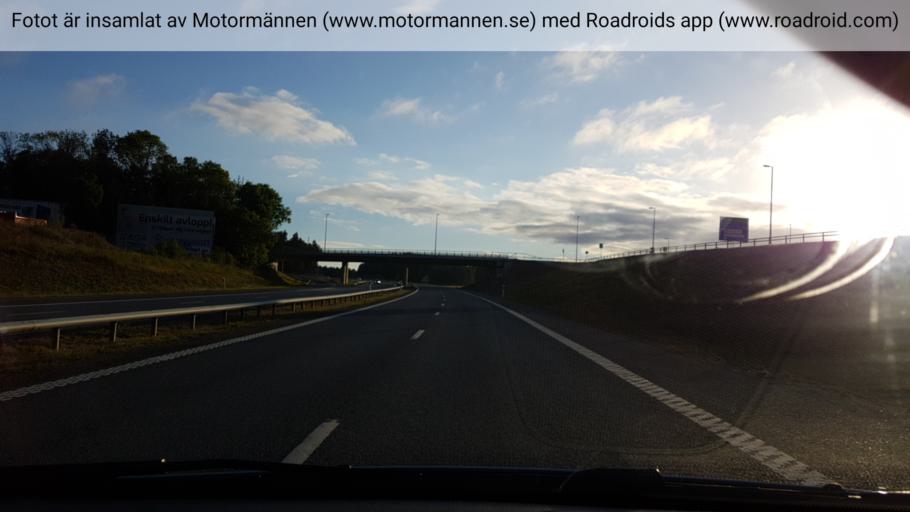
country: SE
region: Stockholm
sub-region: Haninge Kommun
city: Jordbro
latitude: 59.0667
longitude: 18.0609
